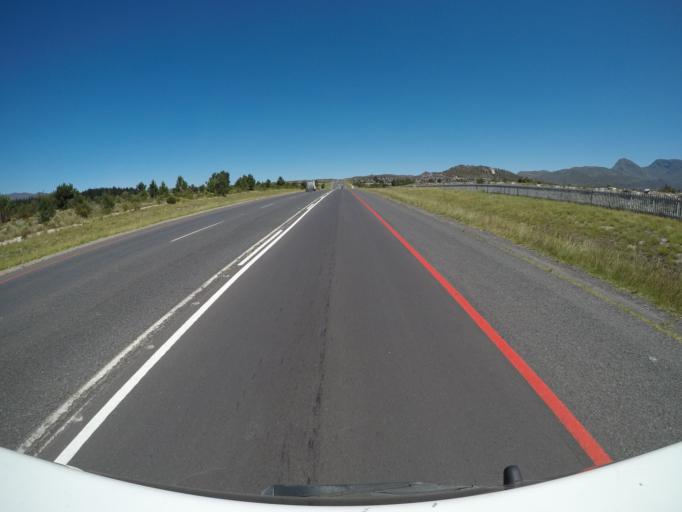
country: ZA
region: Western Cape
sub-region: Overberg District Municipality
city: Grabouw
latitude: -34.1639
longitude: 18.9901
